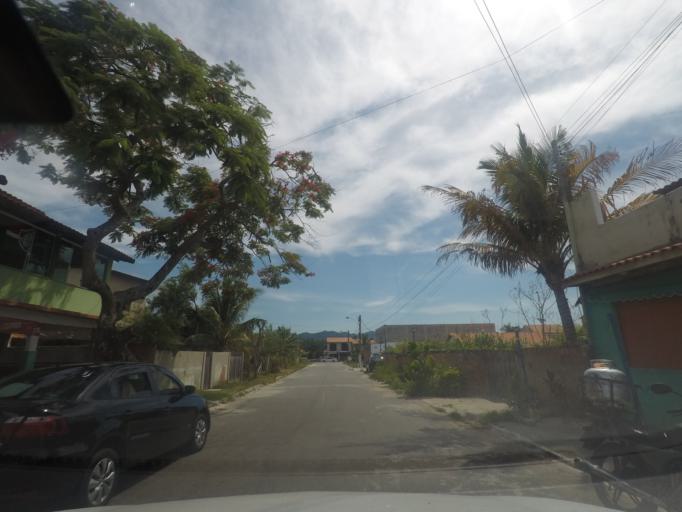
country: BR
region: Rio de Janeiro
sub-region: Marica
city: Marica
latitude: -22.9517
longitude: -42.7499
